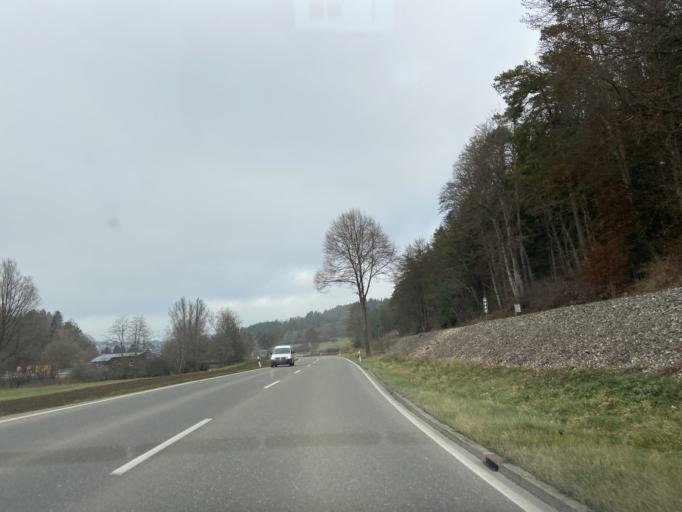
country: DE
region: Baden-Wuerttemberg
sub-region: Tuebingen Region
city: Gammertingen
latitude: 48.2368
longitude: 9.2245
